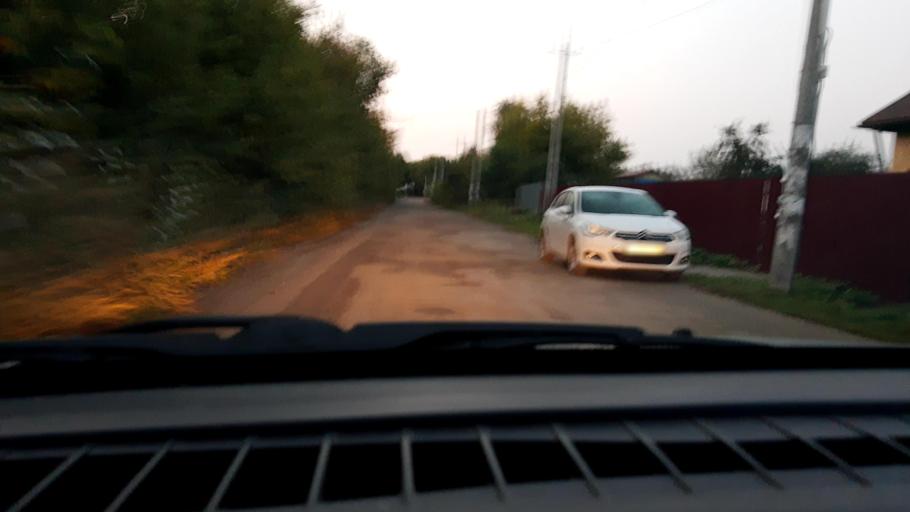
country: RU
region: Nizjnij Novgorod
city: Gorbatovka
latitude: 56.2585
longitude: 43.8287
